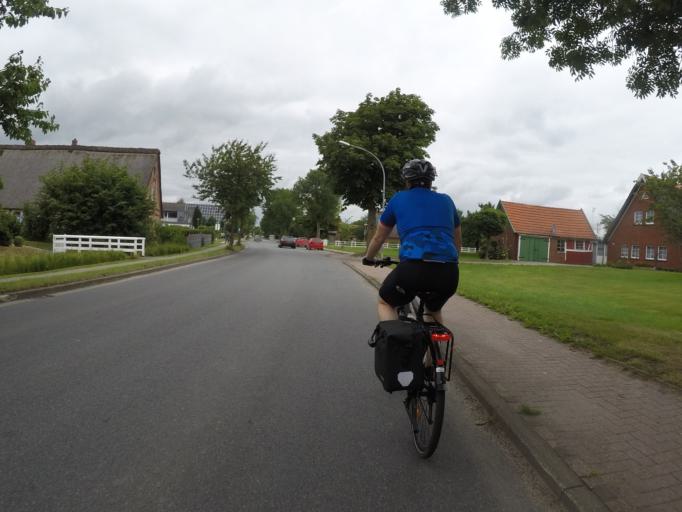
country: DE
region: Lower Saxony
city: Steinkirchen
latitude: 53.5655
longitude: 9.6109
